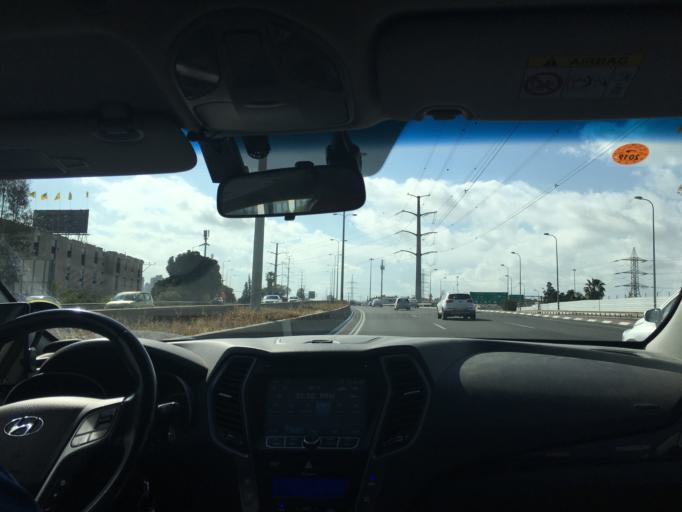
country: IL
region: Tel Aviv
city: Giv`at Shemu'el
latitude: 32.0955
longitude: 34.8459
